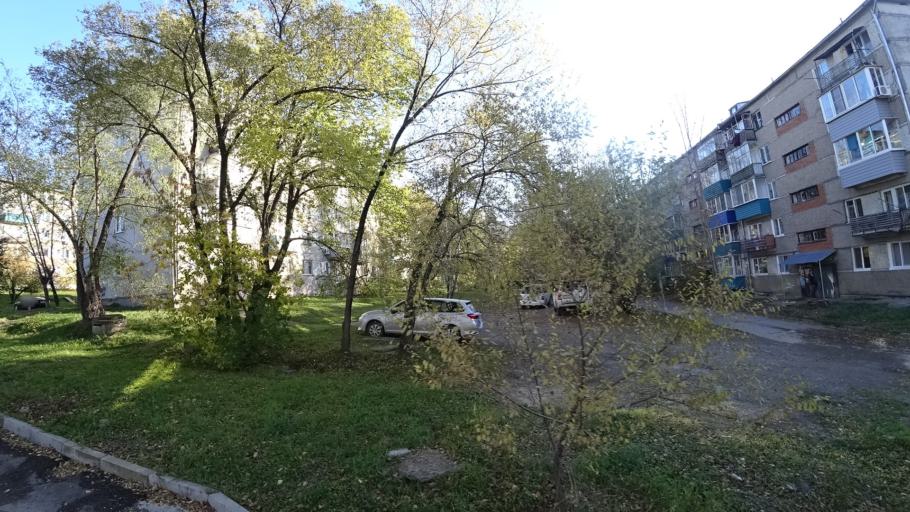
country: RU
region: Khabarovsk Krai
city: Amursk
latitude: 50.2299
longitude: 136.9090
